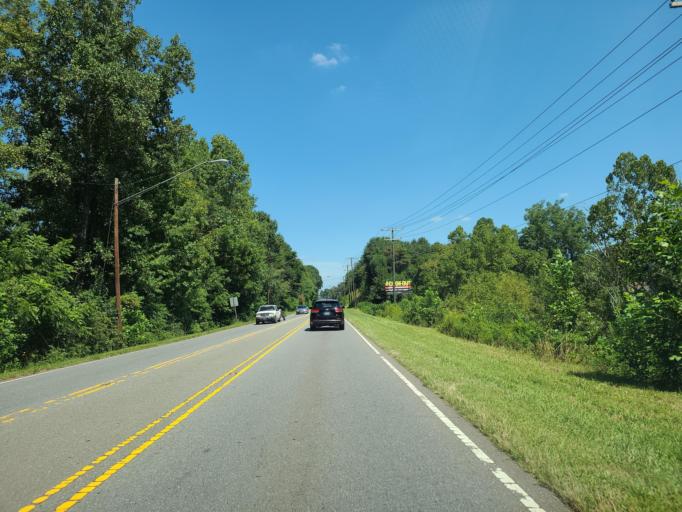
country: US
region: North Carolina
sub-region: Lincoln County
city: Lincolnton
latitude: 35.4625
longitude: -81.2412
